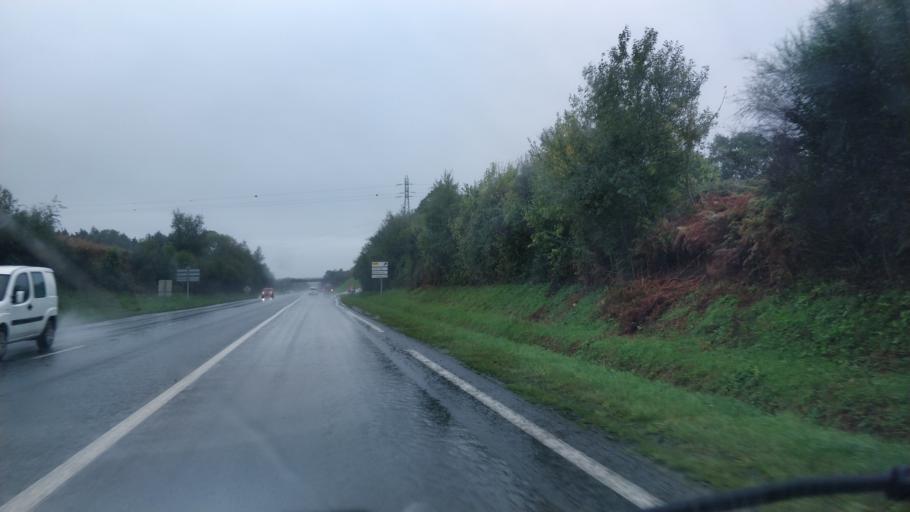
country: FR
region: Lower Normandy
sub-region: Departement de la Manche
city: Saint-Planchers
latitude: 48.8407
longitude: -1.5397
